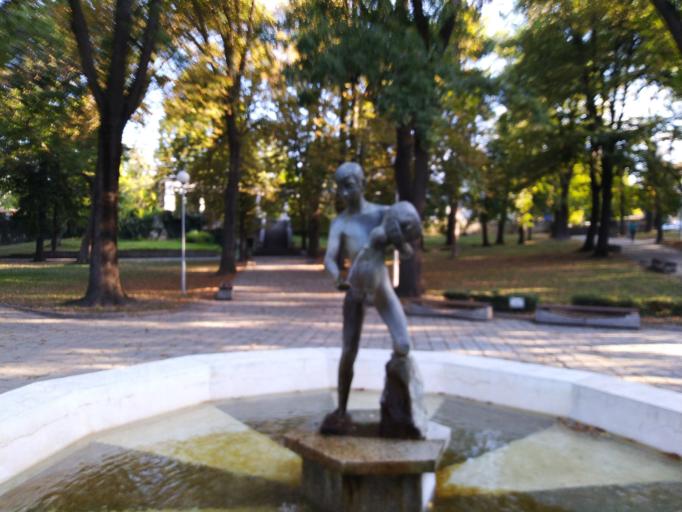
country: BG
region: Plovdiv
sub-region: Obshtina Khisarya
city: Khisarya
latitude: 42.5013
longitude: 24.7035
